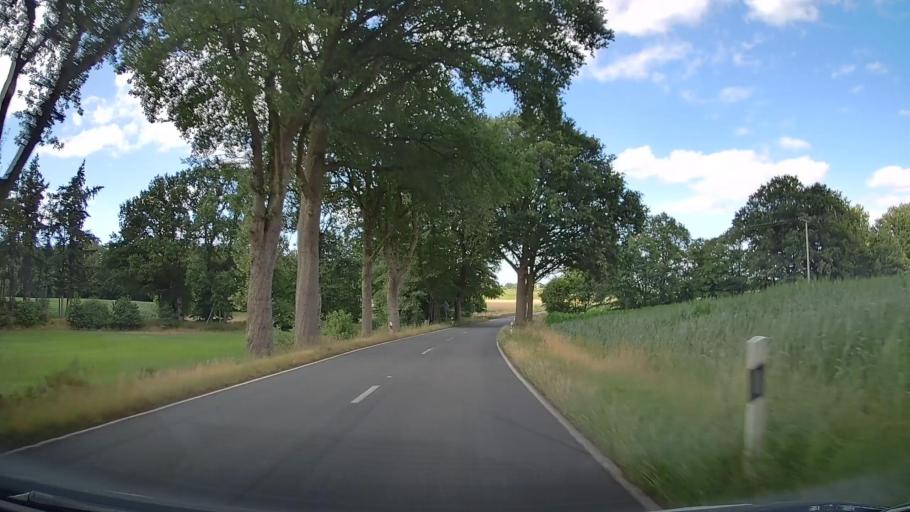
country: DE
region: Lower Saxony
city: Bippen
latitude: 52.6062
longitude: 7.7426
